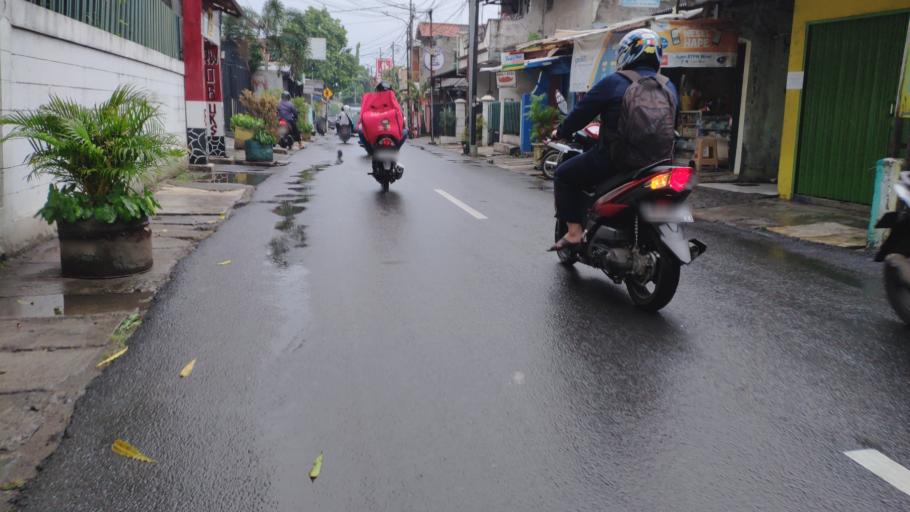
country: ID
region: Jakarta Raya
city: Jakarta
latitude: -6.2044
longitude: 106.8730
